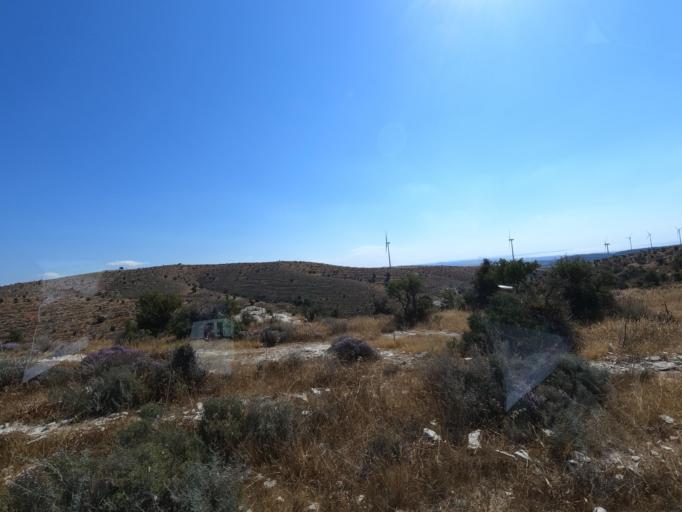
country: CY
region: Larnaka
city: Psevdas
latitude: 34.9630
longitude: 33.4807
